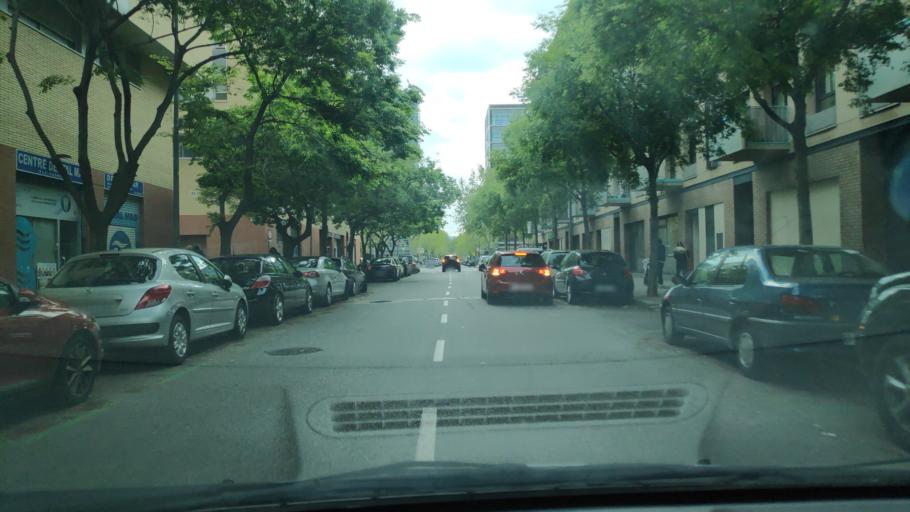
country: ES
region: Catalonia
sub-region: Provincia de Barcelona
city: Sant Marti
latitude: 41.4061
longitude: 2.2105
